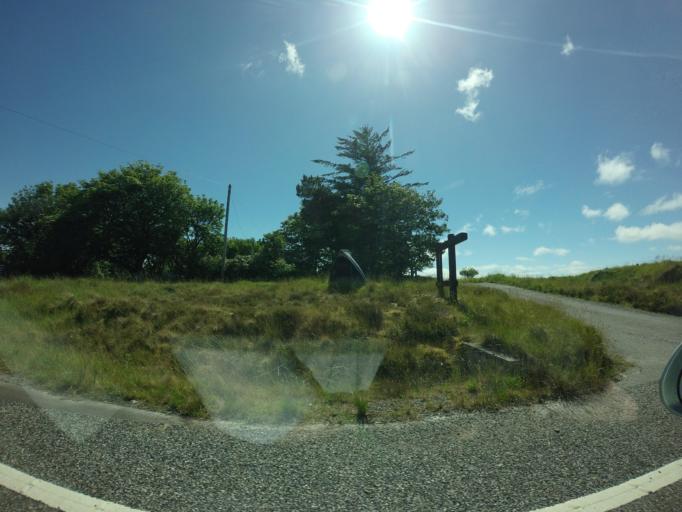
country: GB
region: Scotland
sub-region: Eilean Siar
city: Harris
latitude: 58.1927
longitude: -6.7112
